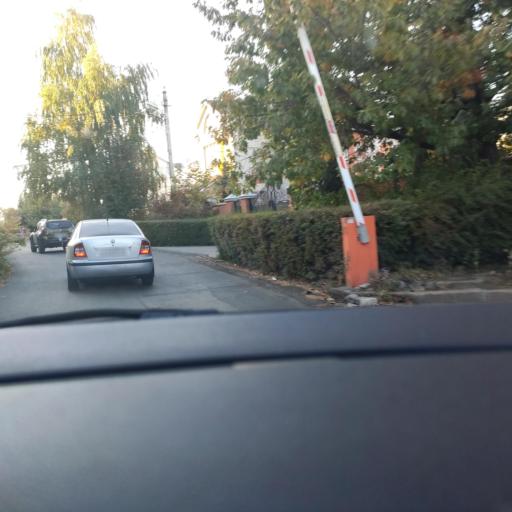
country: RU
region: Voronezj
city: Voronezh
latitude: 51.7073
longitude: 39.2022
